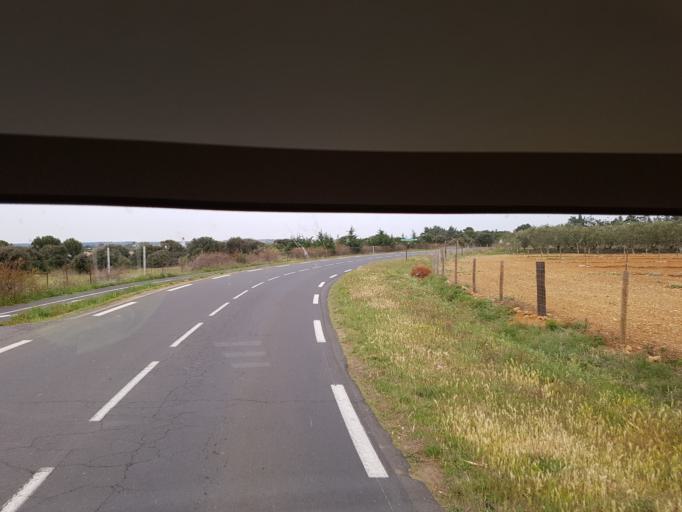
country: FR
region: Languedoc-Roussillon
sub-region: Departement de l'Herault
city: Serignan
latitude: 43.2748
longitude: 3.2644
